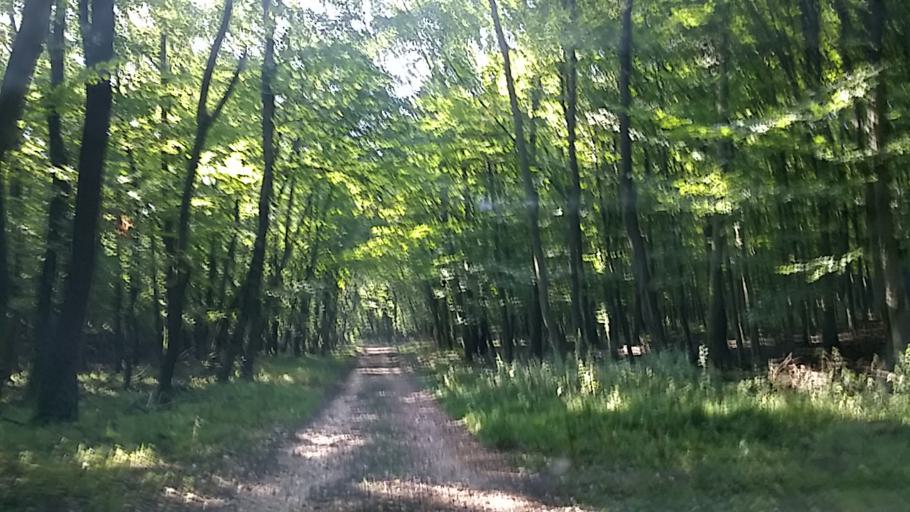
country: HU
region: Komarom-Esztergom
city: Tatabanya
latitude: 47.5944
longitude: 18.4308
